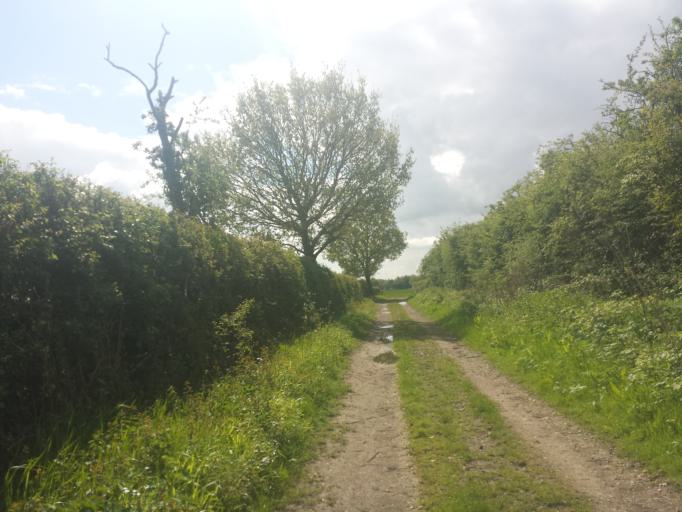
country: GB
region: England
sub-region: Essex
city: Great Bentley
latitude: 51.8796
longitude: 1.0453
